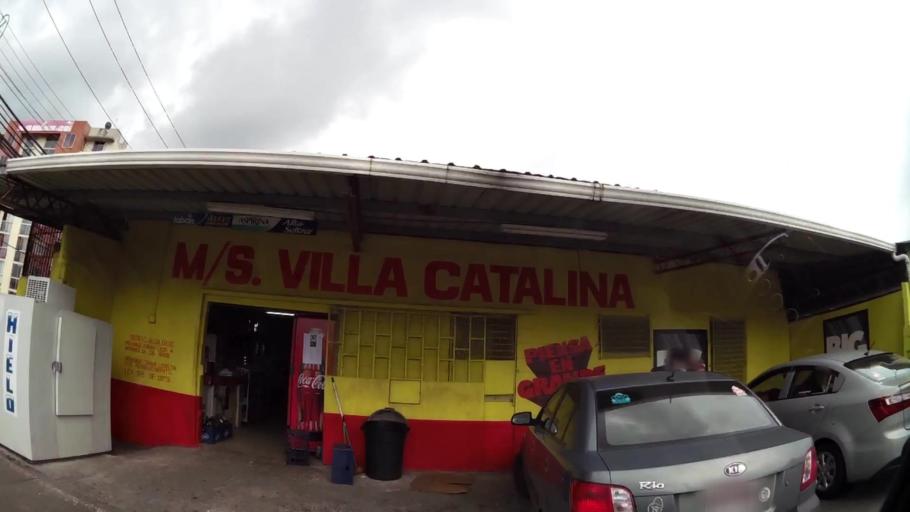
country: PA
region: Panama
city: Tocumen
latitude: 9.0630
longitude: -79.4176
